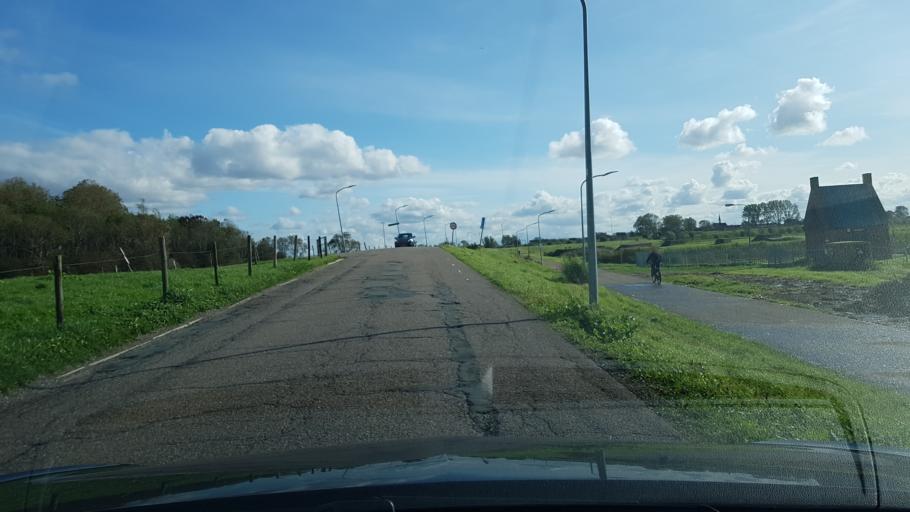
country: NL
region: North Holland
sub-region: Gemeente Velsen
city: Velsen-Zuid
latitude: 52.4207
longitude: 4.6709
